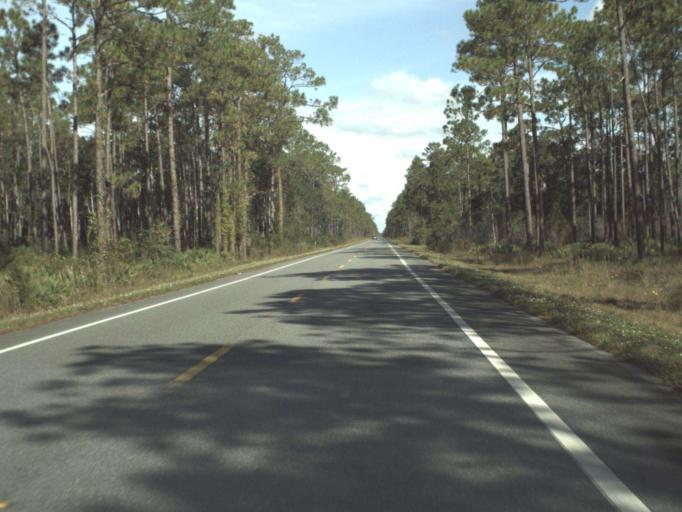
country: US
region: Florida
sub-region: Franklin County
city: Apalachicola
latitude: 29.9808
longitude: -84.9755
